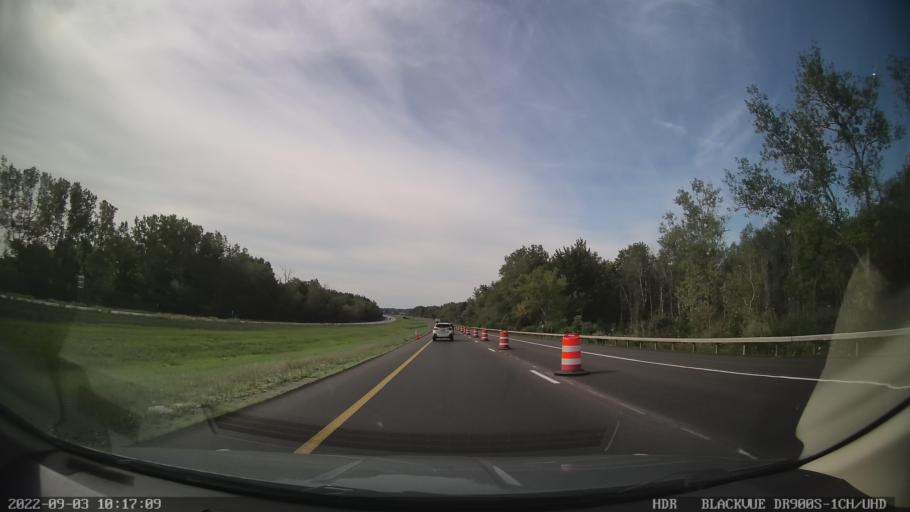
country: US
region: New York
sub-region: Livingston County
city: Avon
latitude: 42.9669
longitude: -77.6915
